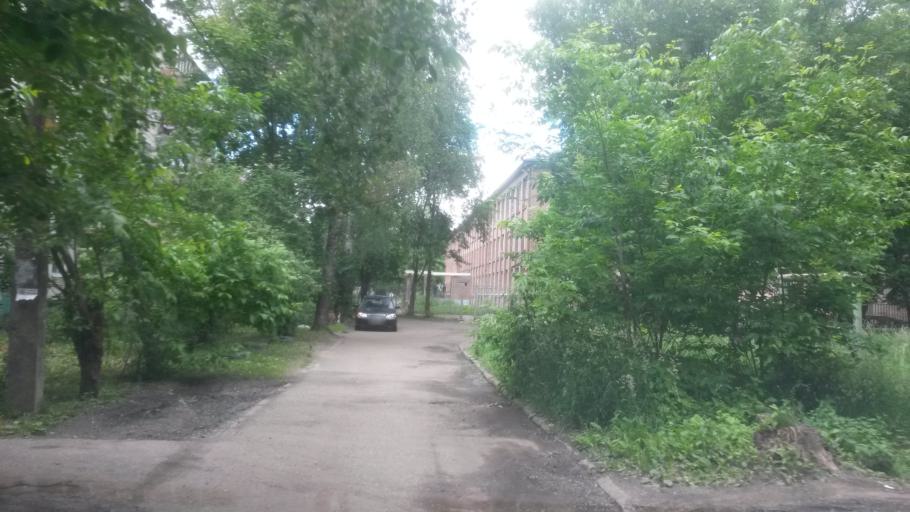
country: RU
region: Jaroslavl
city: Yaroslavl
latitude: 57.6843
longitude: 39.8121
